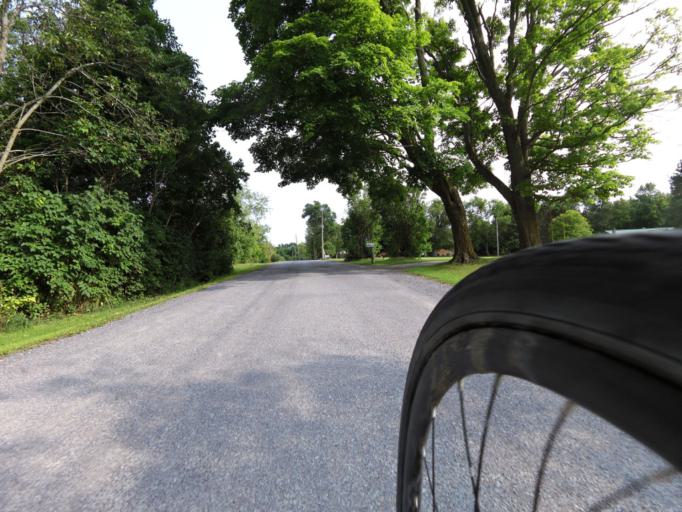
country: CA
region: Ontario
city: Quinte West
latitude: 44.0493
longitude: -77.6293
